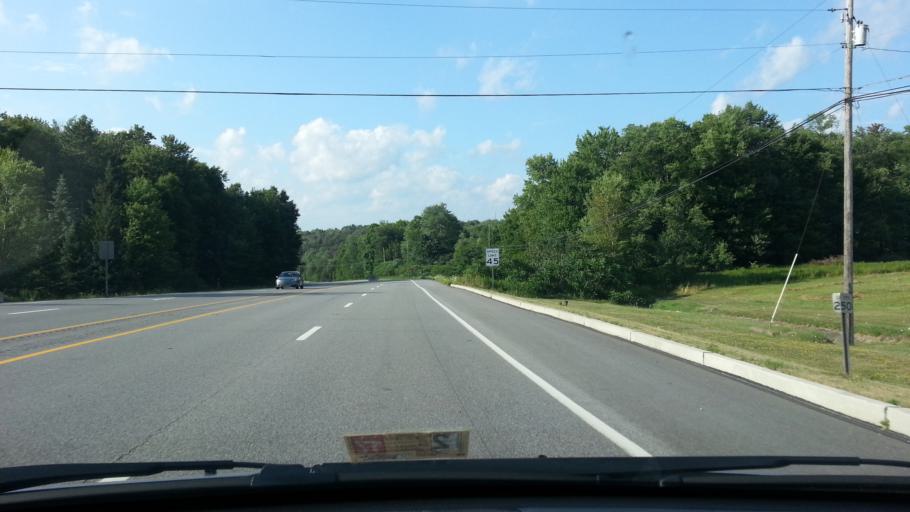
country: US
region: Pennsylvania
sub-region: Elk County
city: Saint Marys
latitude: 41.3797
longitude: -78.5588
